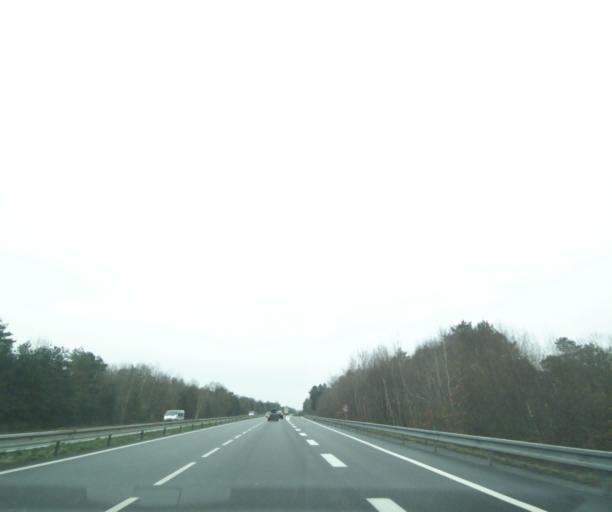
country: FR
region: Centre
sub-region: Departement du Loir-et-Cher
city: Salbris
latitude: 47.4732
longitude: 2.0086
